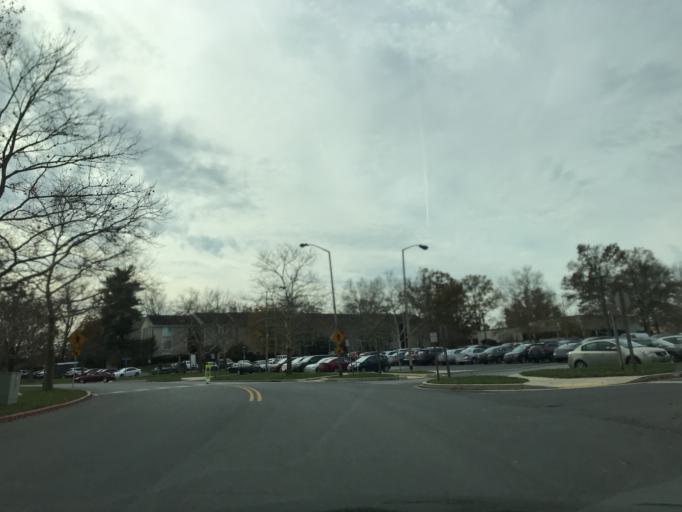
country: US
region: Maryland
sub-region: Howard County
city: Riverside
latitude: 39.2232
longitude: -76.8868
